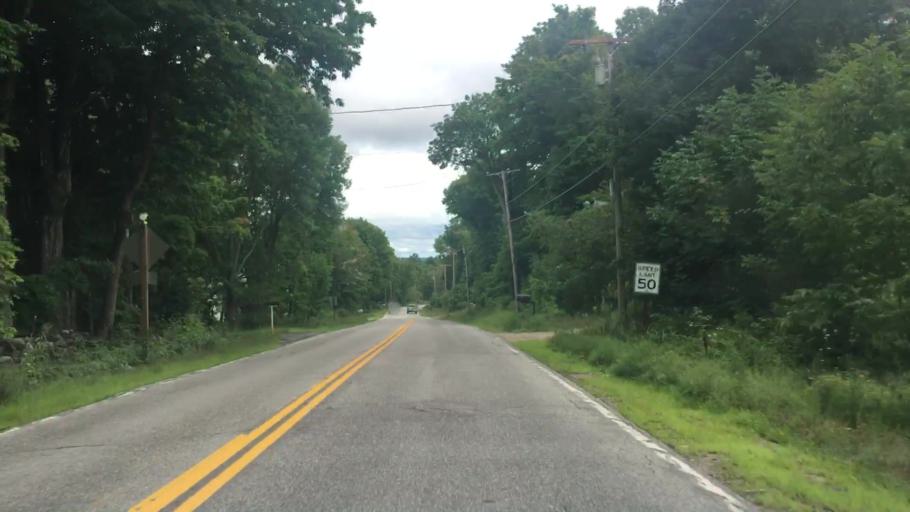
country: US
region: Maine
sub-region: York County
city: Limerick
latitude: 43.6782
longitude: -70.7860
